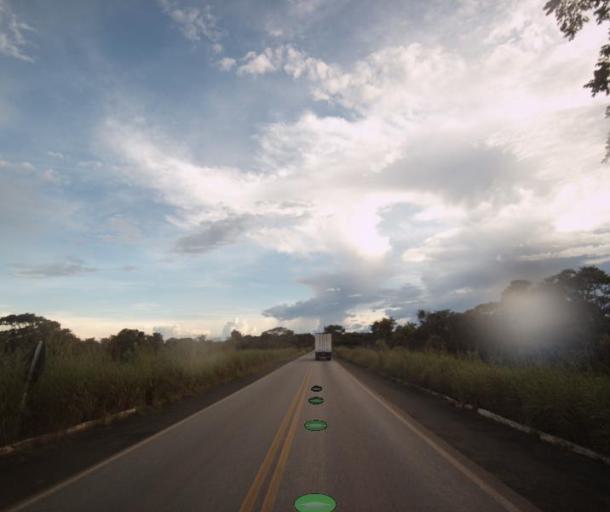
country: BR
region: Goias
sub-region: Uruacu
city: Uruacu
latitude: -14.0612
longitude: -49.0923
